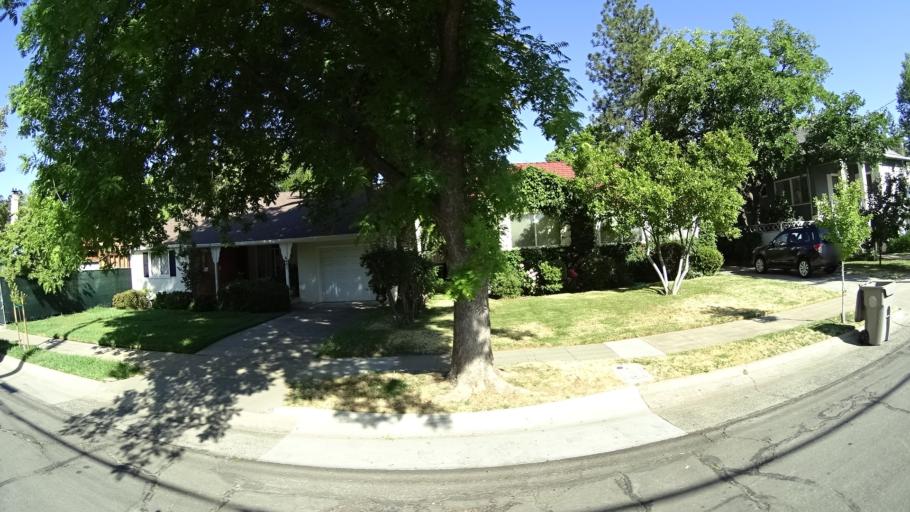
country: US
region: California
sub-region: Sacramento County
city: Sacramento
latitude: 38.5727
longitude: -121.4486
